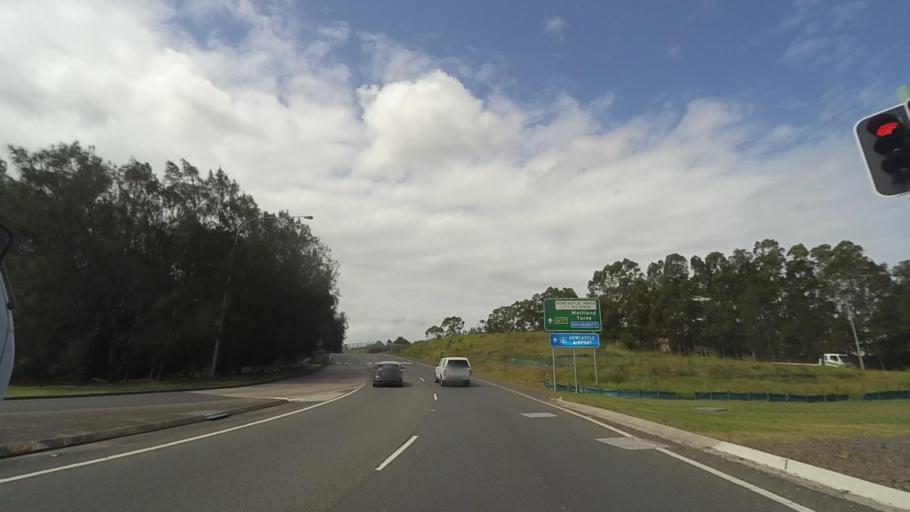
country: AU
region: New South Wales
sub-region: Newcastle
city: North Lambton
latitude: -32.9056
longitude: 151.6924
